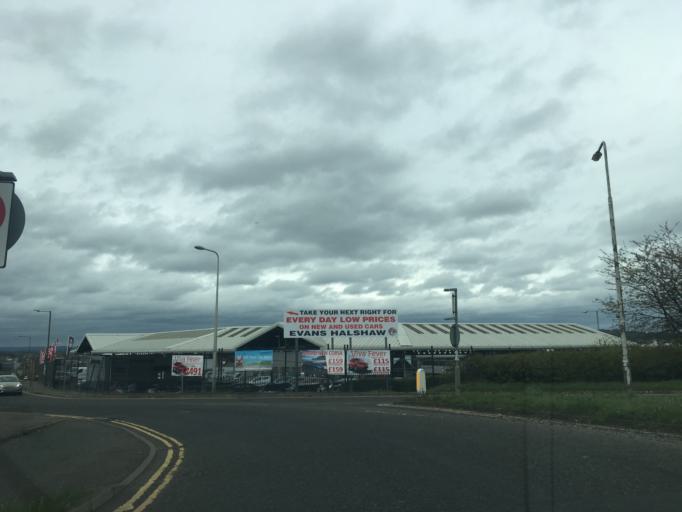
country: GB
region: Scotland
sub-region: Edinburgh
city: Currie
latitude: 55.9206
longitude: -3.3016
